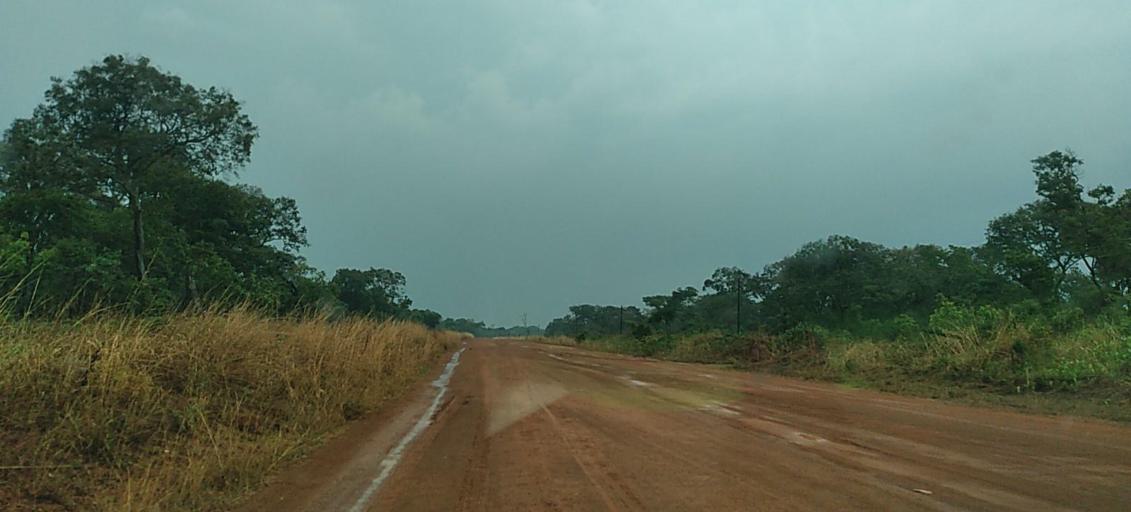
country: ZM
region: North-Western
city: Mwinilunga
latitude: -11.6122
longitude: 24.3989
